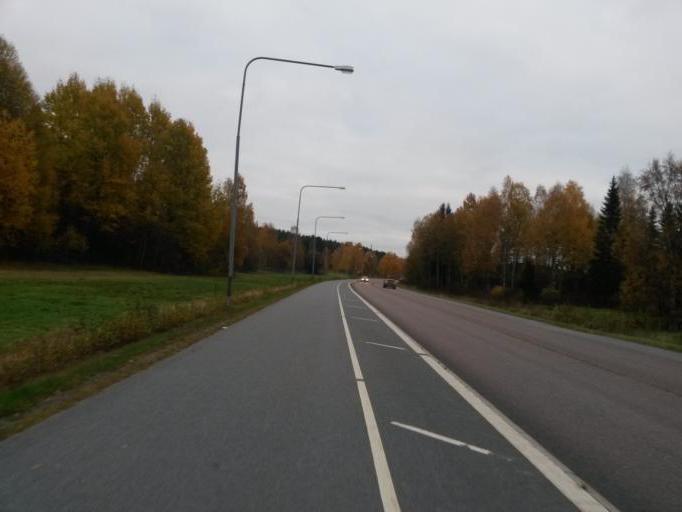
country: SE
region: Vaesterbotten
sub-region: Skelleftea Kommun
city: Skelleftea
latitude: 64.7554
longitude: 20.9905
